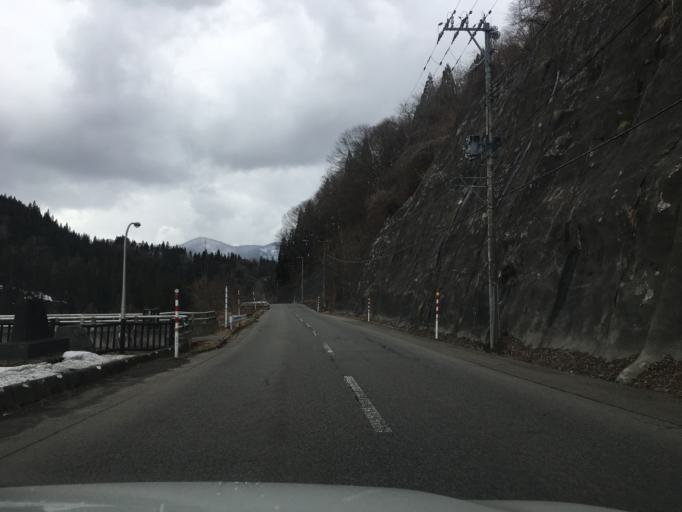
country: JP
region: Akita
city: Odate
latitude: 40.4278
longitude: 140.6500
